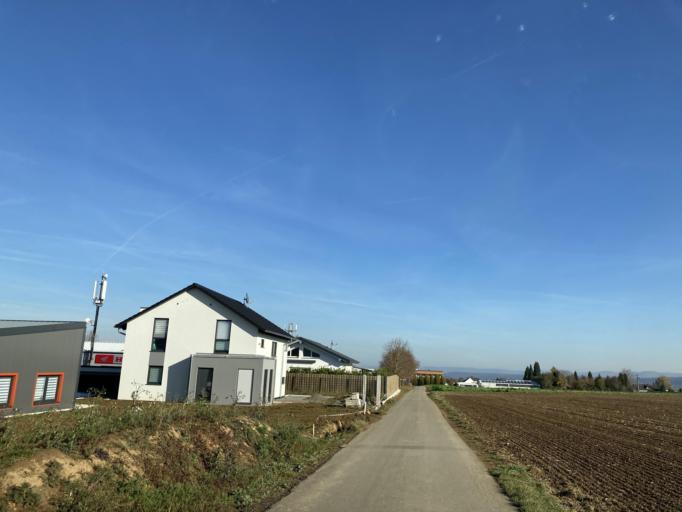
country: DE
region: Baden-Wuerttemberg
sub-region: Regierungsbezirk Stuttgart
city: Bondorf
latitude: 48.4805
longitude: 8.8721
